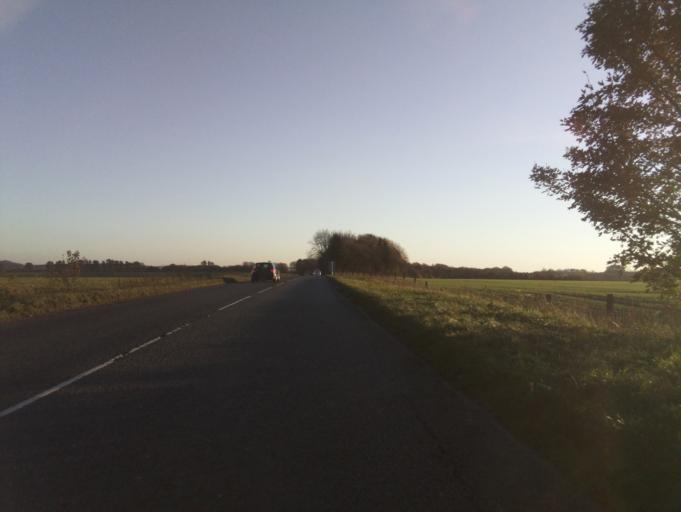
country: GB
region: England
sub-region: Wiltshire
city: Chicklade
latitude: 51.1157
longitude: -2.1693
